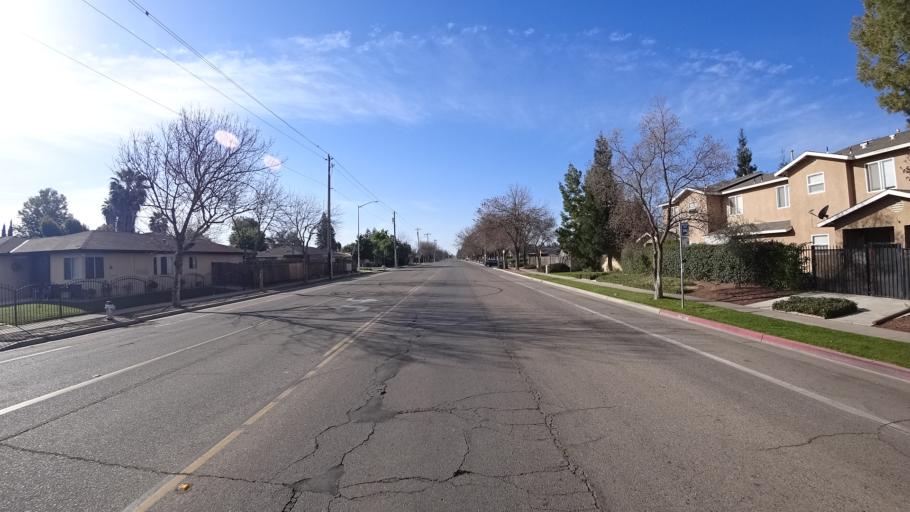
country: US
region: California
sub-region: Fresno County
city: West Park
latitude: 36.7993
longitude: -119.8805
